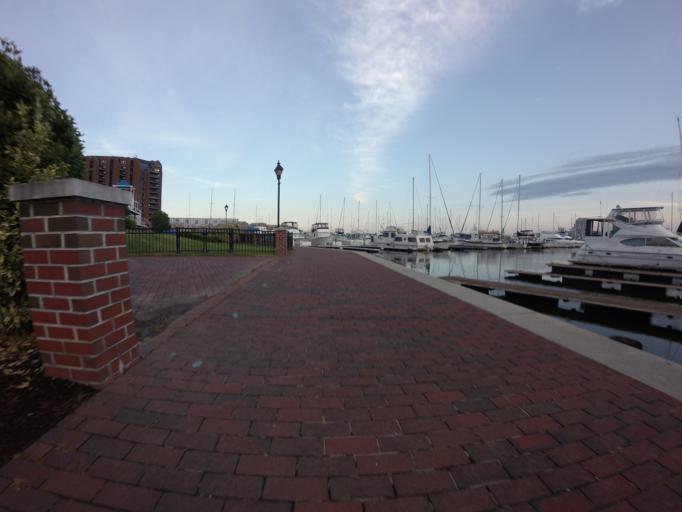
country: US
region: Maryland
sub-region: City of Baltimore
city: Baltimore
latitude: 39.2810
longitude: -76.5826
